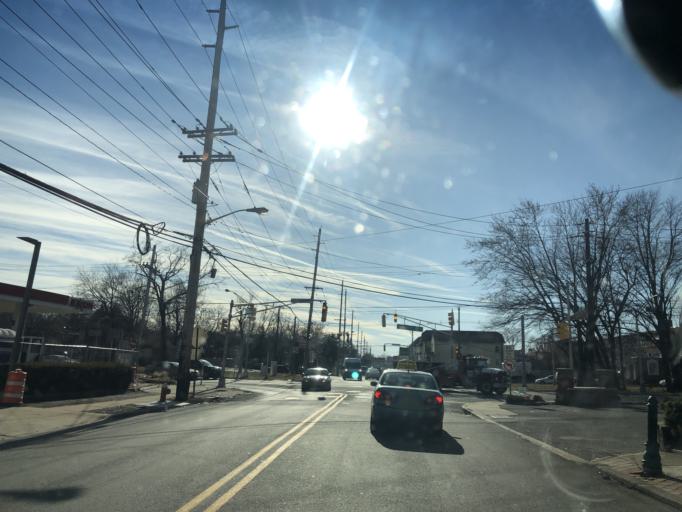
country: US
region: New Jersey
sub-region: Bergen County
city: Fair Lawn
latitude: 40.9235
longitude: -74.1408
